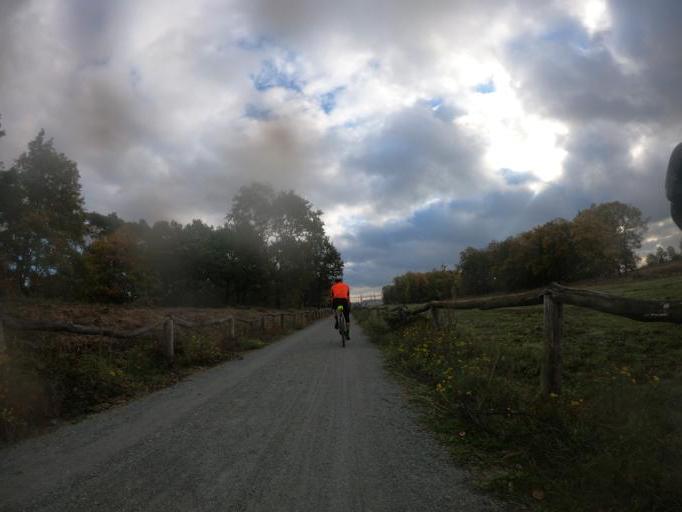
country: DE
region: Hesse
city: Kelsterbach
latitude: 50.0490
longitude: 8.5257
